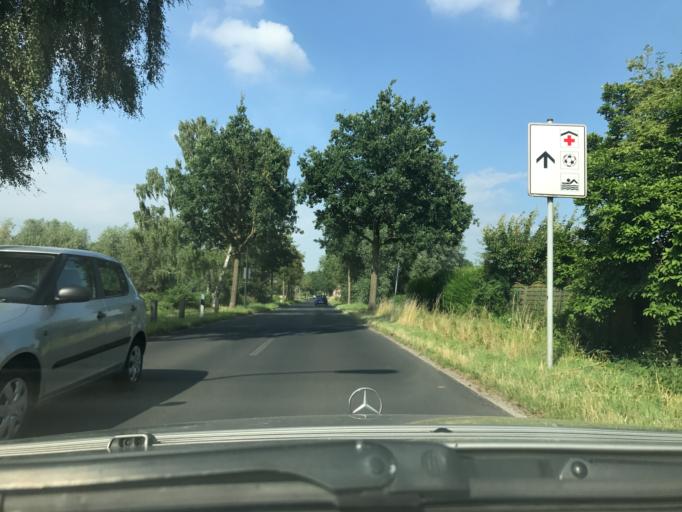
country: DE
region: North Rhine-Westphalia
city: Tonisvorst
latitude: 51.3692
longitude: 6.5210
